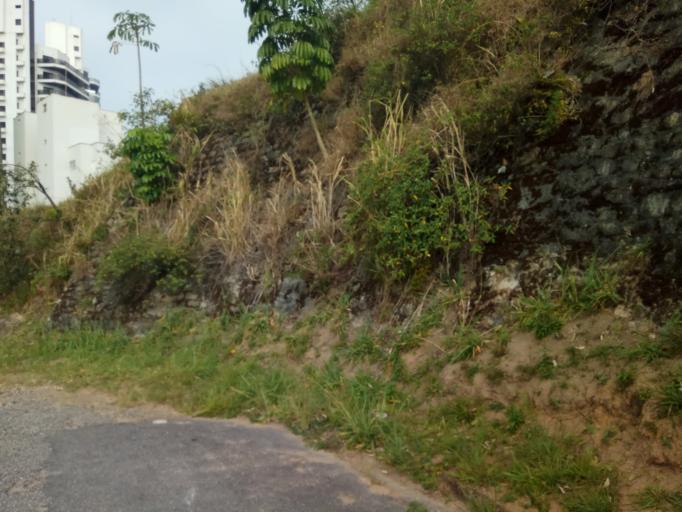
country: BR
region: Sao Paulo
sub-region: Guaruja
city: Guaruja
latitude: -24.0129
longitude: -46.2657
